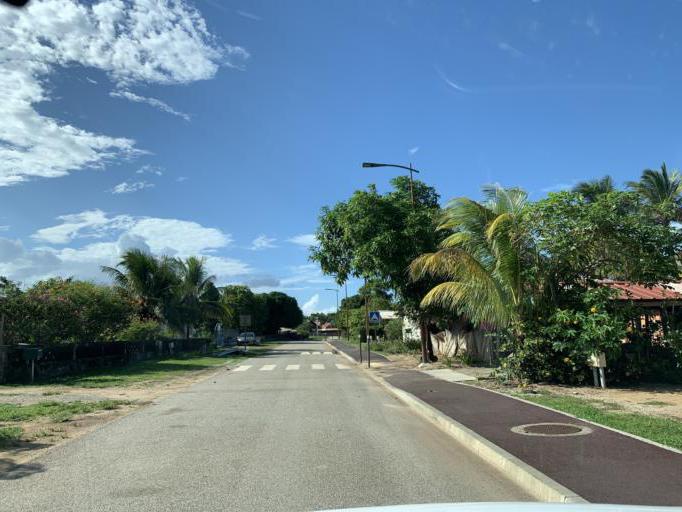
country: GF
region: Guyane
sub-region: Guyane
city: Kourou
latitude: 5.1732
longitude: -52.6451
